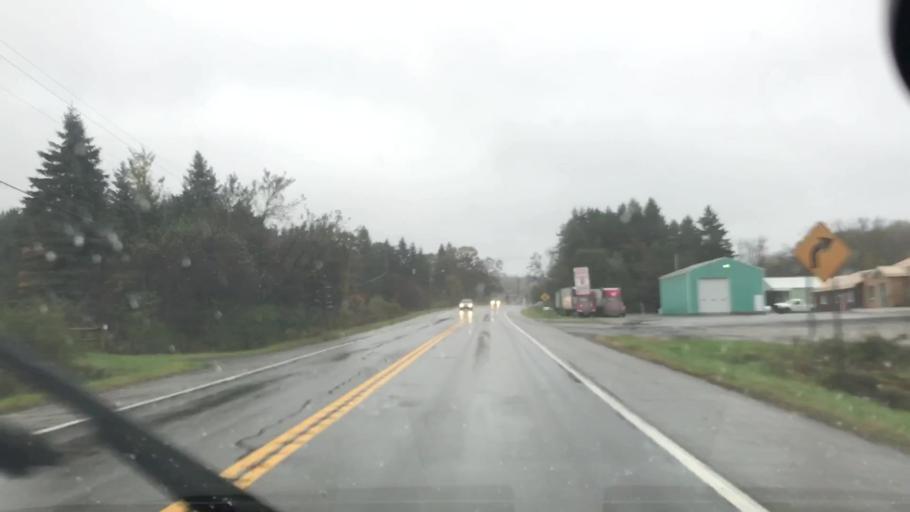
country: US
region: New York
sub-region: Erie County
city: Springville
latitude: 42.3990
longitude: -78.6790
